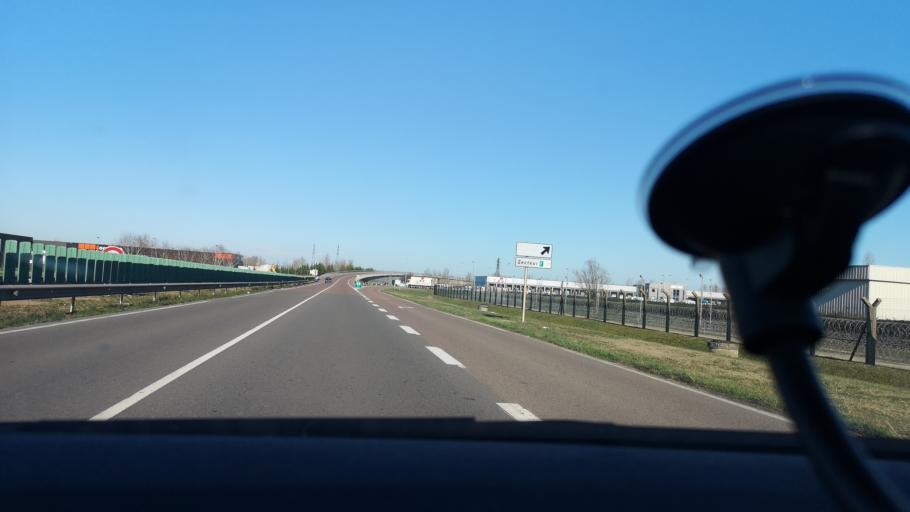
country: FR
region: Bourgogne
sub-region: Departement de Saone-et-Loire
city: Saint-Marcel
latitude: 46.7667
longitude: 4.8707
